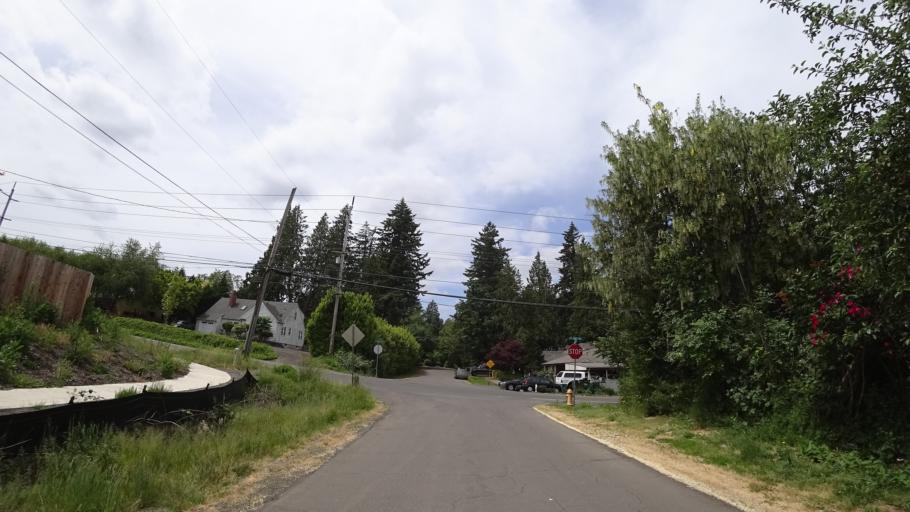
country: US
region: Oregon
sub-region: Washington County
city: Metzger
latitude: 45.4493
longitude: -122.7587
